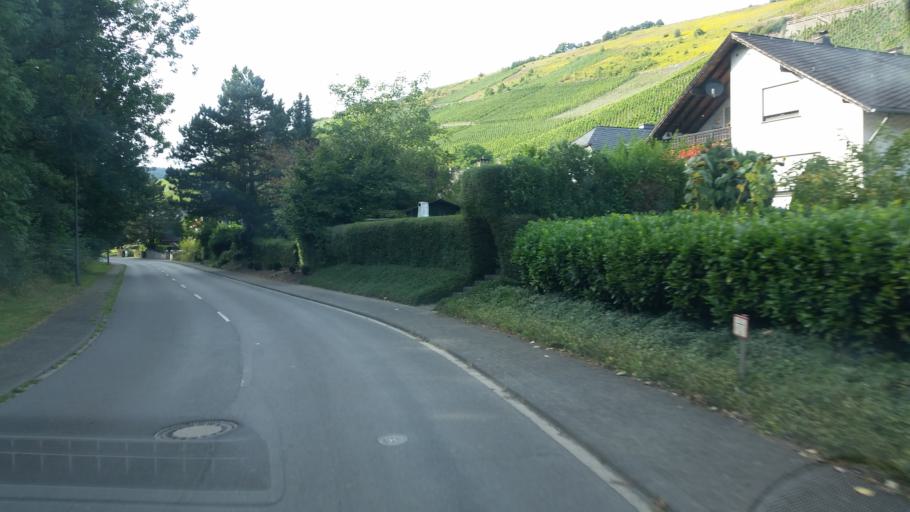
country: DE
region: Rheinland-Pfalz
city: Starkenburg
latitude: 49.9824
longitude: 7.1386
